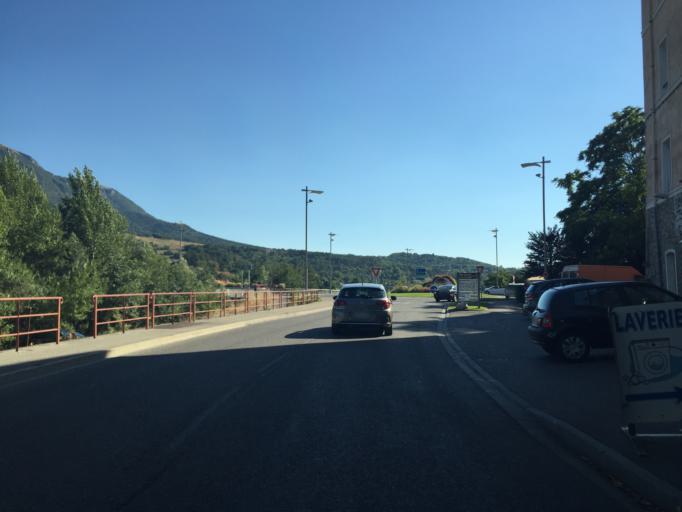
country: FR
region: Provence-Alpes-Cote d'Azur
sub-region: Departement des Alpes-de-Haute-Provence
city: Digne-les-Bains
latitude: 44.0902
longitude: 6.2283
